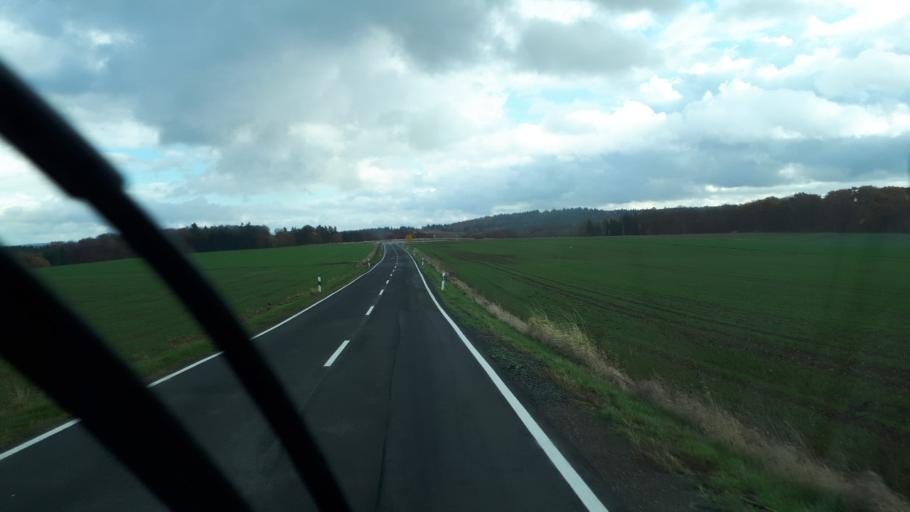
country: DE
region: Rheinland-Pfalz
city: Brohl
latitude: 50.2083
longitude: 7.2719
